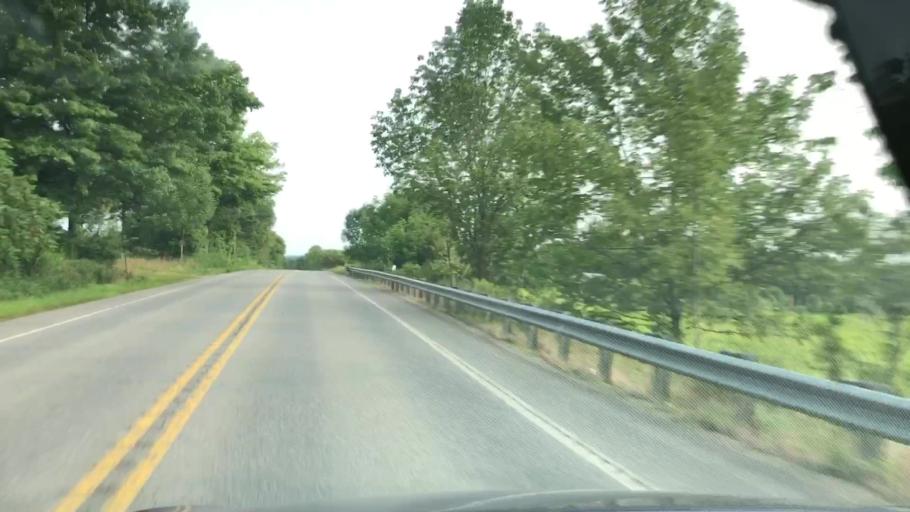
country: US
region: Pennsylvania
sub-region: Erie County
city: Union City
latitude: 41.8441
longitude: -79.8224
